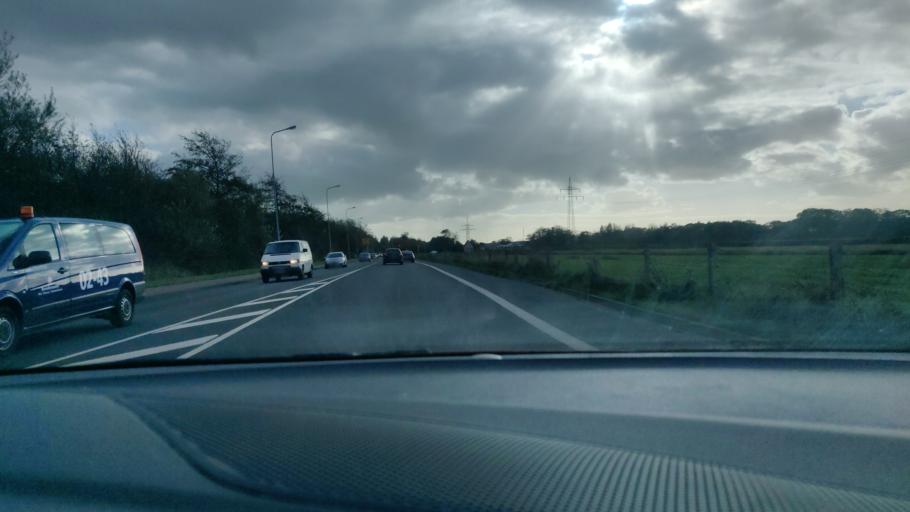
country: DE
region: Lower Saxony
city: Cuxhaven
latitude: 53.8639
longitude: 8.6747
